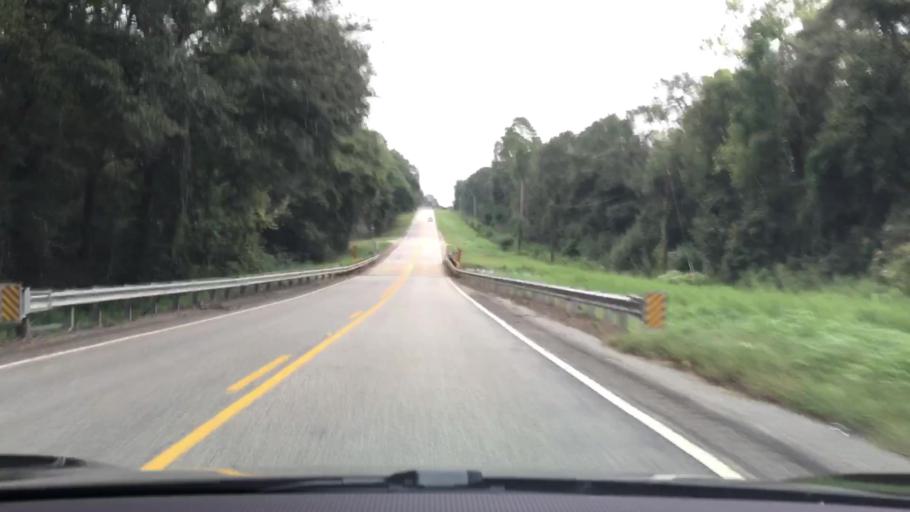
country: US
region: Alabama
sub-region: Covington County
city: Opp
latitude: 31.2957
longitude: -86.1434
